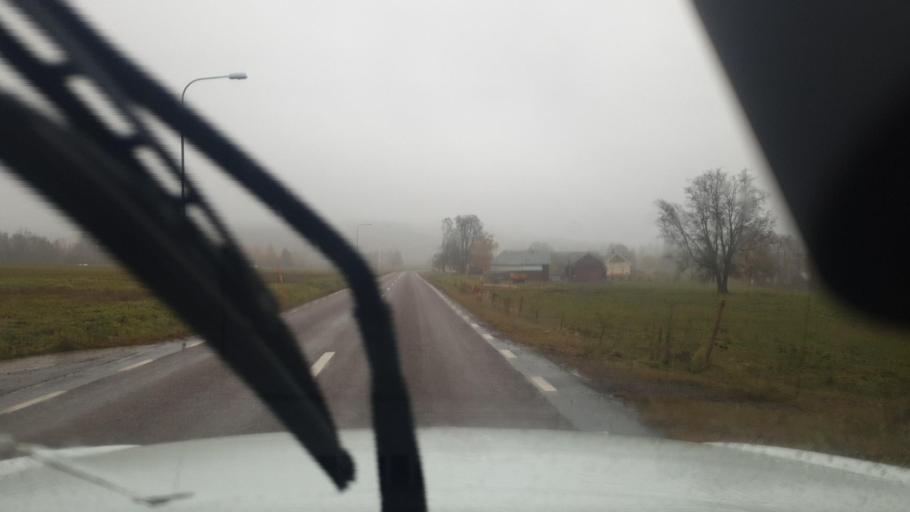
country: SE
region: Vaermland
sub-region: Sunne Kommun
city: Sunne
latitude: 59.8456
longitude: 12.9471
